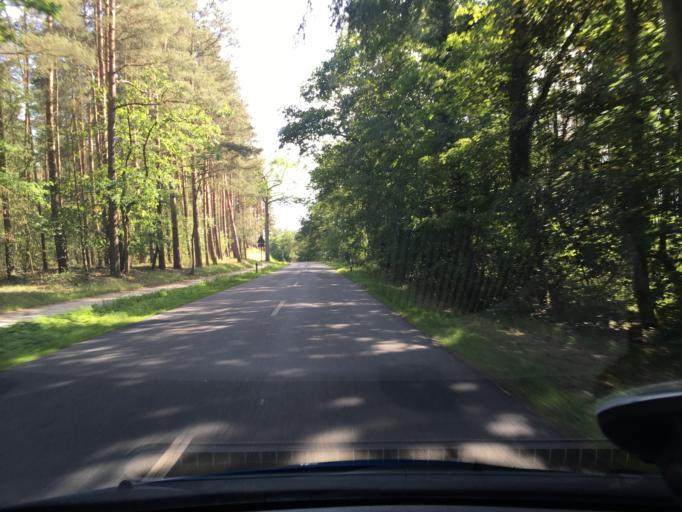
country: DE
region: Lower Saxony
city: Neu Darchau
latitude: 53.2946
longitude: 10.9291
